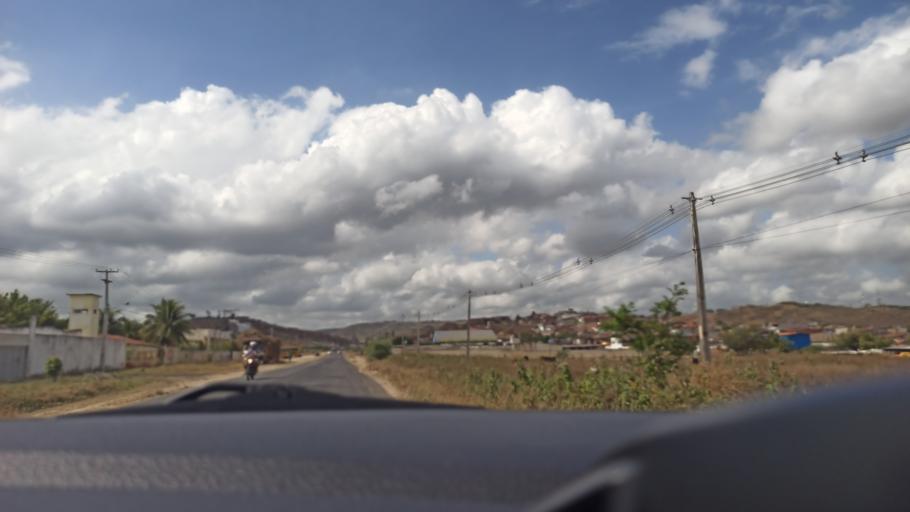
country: BR
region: Pernambuco
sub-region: Timbauba
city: Timbauba
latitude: -7.4976
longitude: -35.2980
